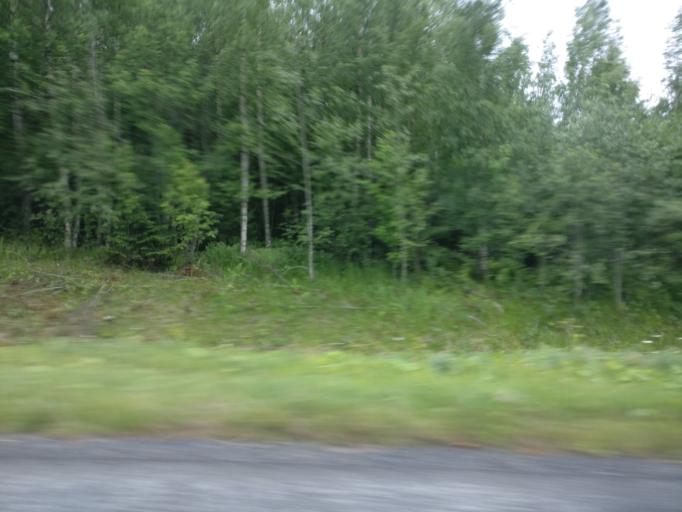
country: FI
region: Northern Savo
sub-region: Kuopio
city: Kuopio
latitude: 62.9768
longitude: 27.8036
